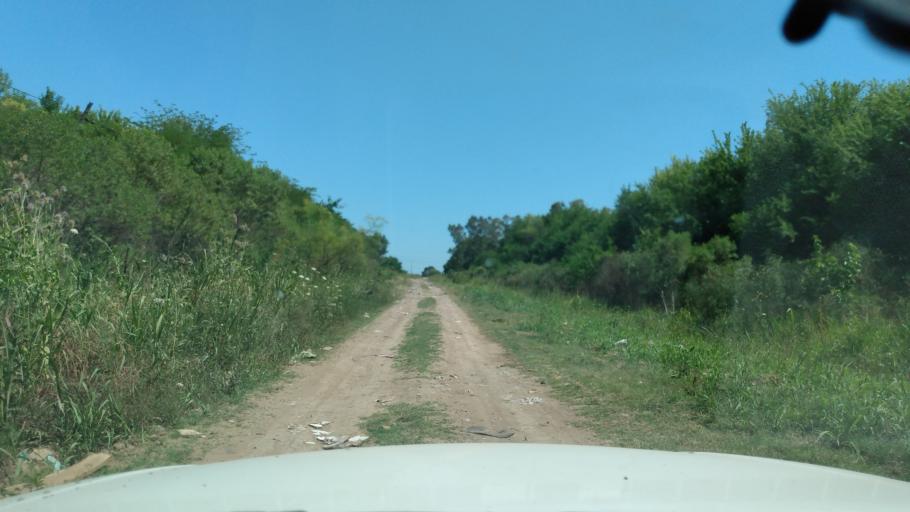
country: AR
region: Buenos Aires
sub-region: Partido de Lujan
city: Lujan
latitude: -34.5518
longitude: -59.1402
